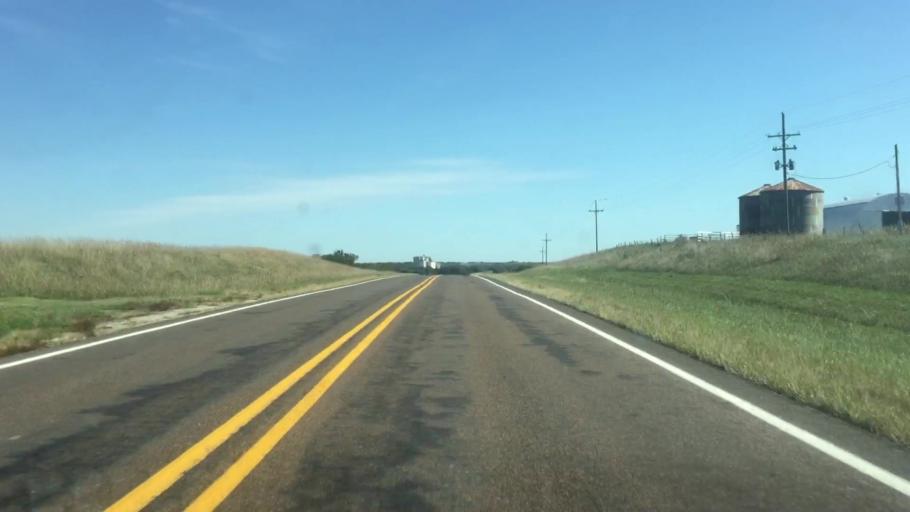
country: US
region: Nebraska
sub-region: Gage County
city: Wymore
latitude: 40.0458
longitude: -96.8298
